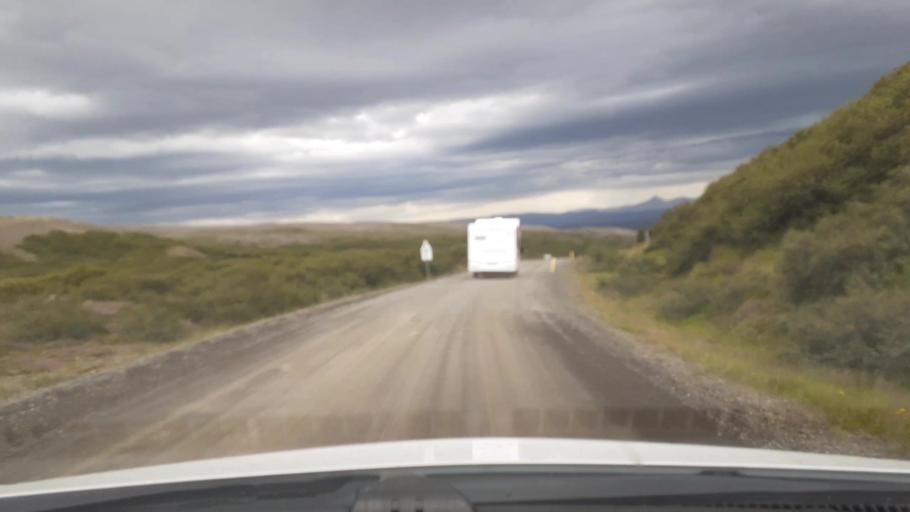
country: IS
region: West
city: Borgarnes
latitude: 64.5593
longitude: -21.6265
